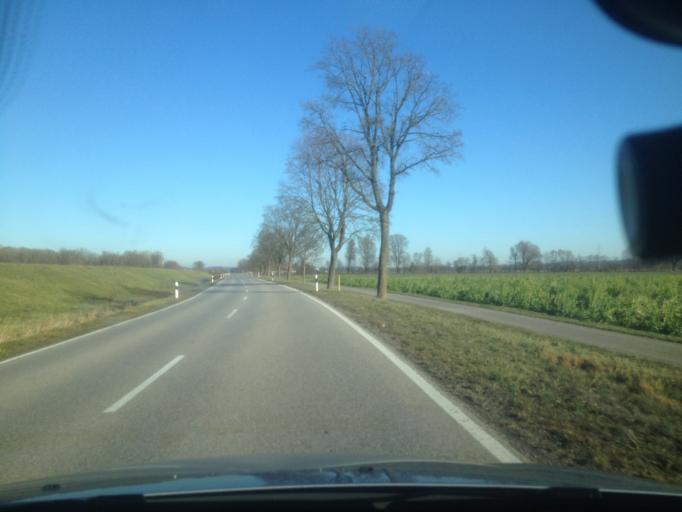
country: DE
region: Bavaria
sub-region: Upper Bavaria
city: Langenpreising
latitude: 48.4431
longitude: 11.9418
